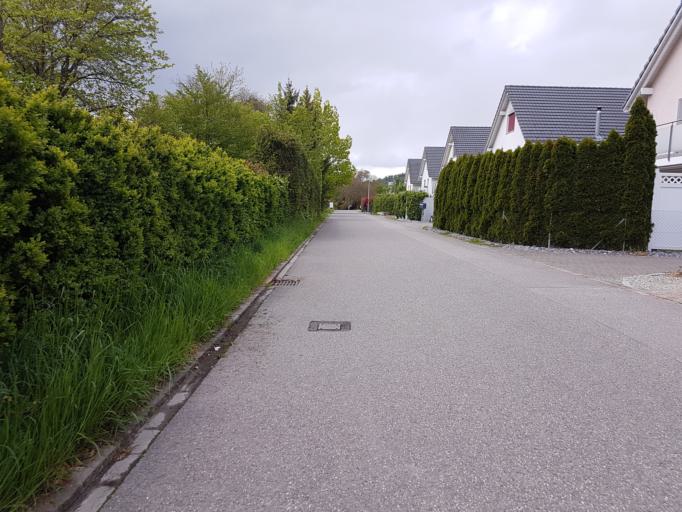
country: CH
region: Aargau
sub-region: Bezirk Brugg
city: Rupperswil
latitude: 47.4152
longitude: 8.1445
